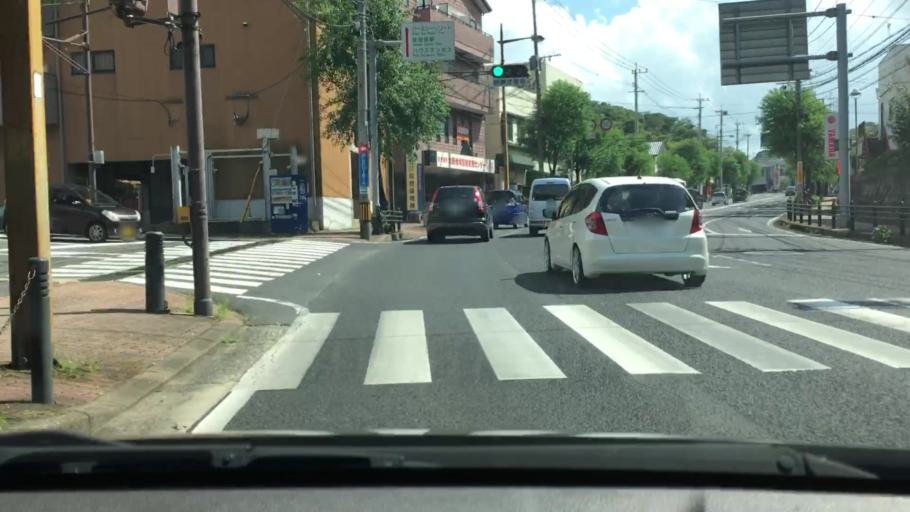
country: JP
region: Nagasaki
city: Sasebo
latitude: 33.2040
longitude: 129.7213
